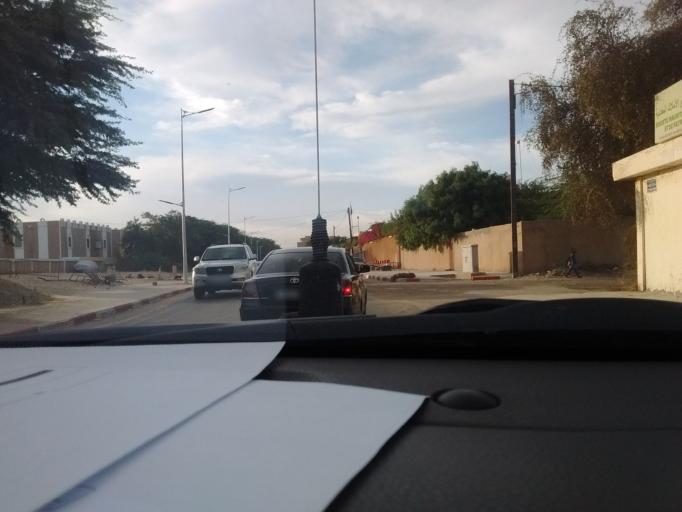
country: MR
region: Nouakchott
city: Nouakchott
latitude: 18.0908
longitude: -15.9834
